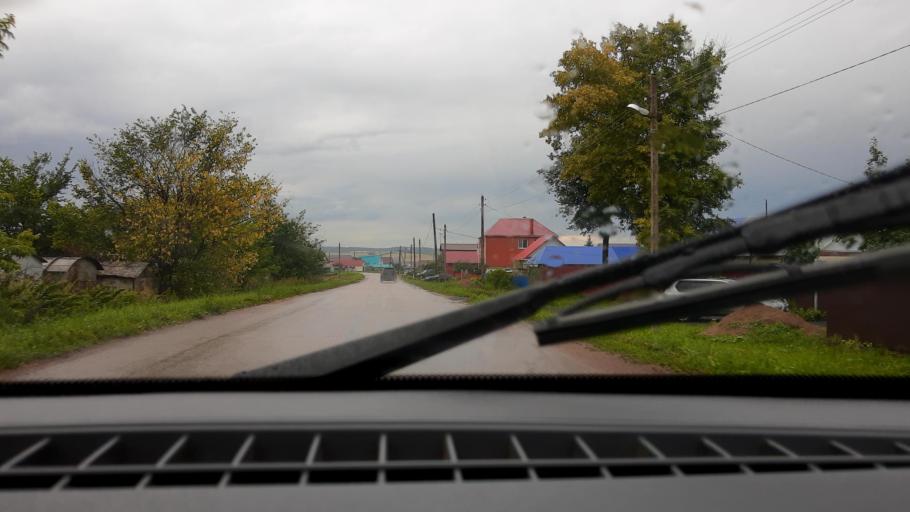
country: RU
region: Bashkortostan
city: Avdon
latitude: 54.8163
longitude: 55.6959
